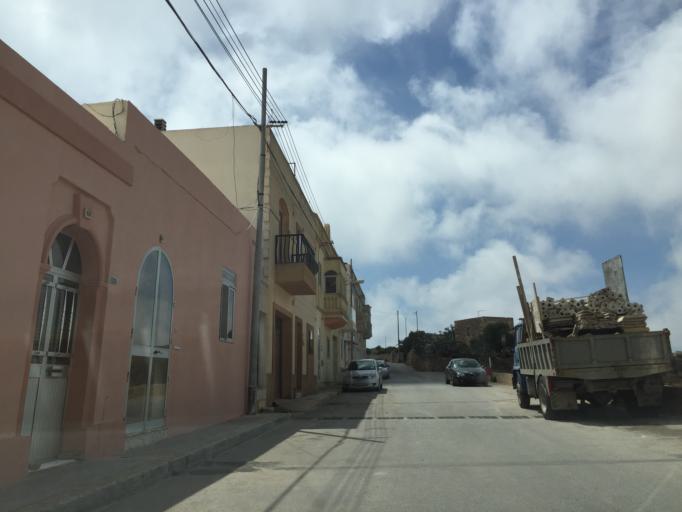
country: MT
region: Dingli
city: Dingli
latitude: 35.8604
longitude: 14.3765
